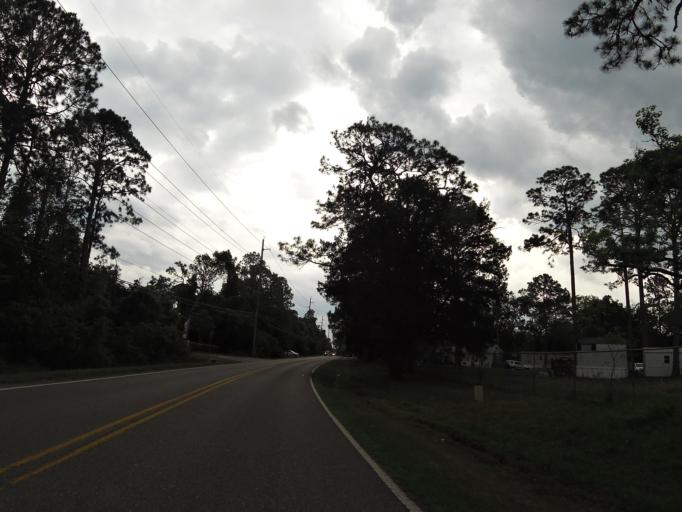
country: US
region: Florida
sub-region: Clay County
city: Bellair-Meadowbrook Terrace
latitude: 30.1982
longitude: -81.7184
